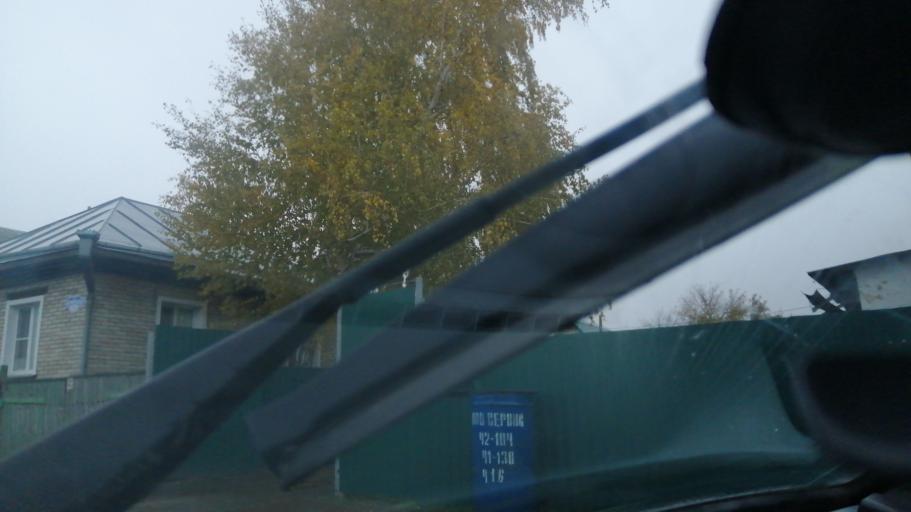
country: RU
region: Novosibirsk
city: Krasnozerskoye
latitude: 53.9731
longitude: 79.2469
